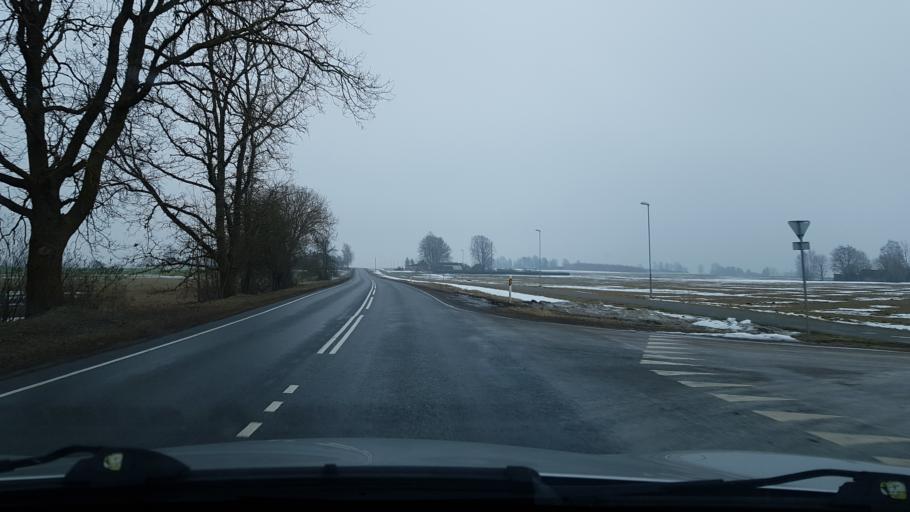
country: EE
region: Valgamaa
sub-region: Torva linn
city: Torva
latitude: 58.2258
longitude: 25.8884
